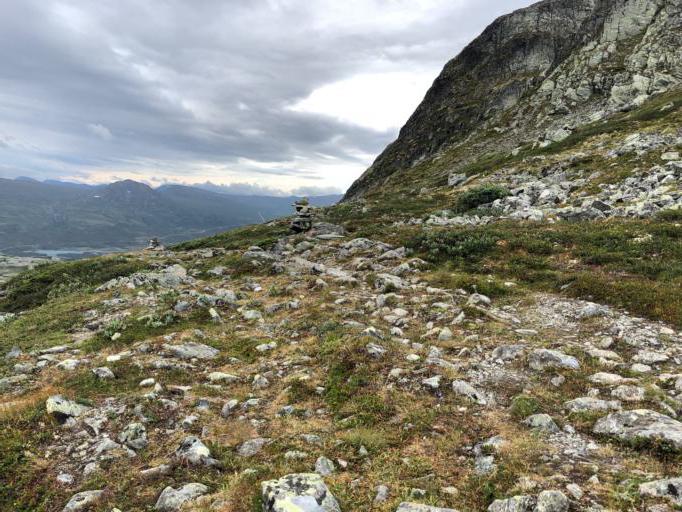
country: NO
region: Oppland
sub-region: Lom
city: Fossbergom
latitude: 61.5147
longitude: 8.8148
